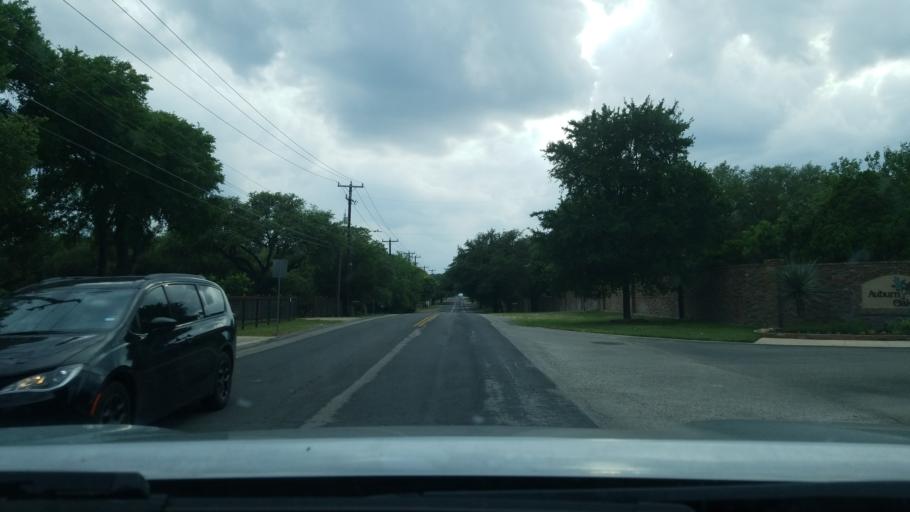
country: US
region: Texas
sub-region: Bexar County
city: Shavano Park
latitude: 29.5448
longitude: -98.5909
